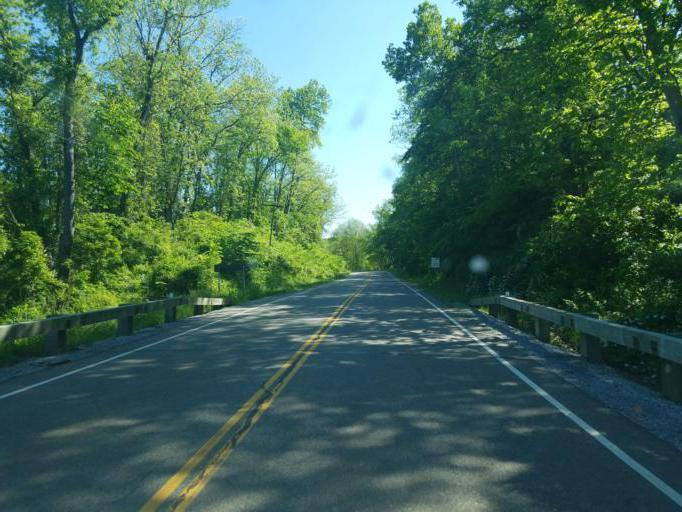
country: US
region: Ohio
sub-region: Summit County
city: Peninsula
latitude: 41.2184
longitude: -81.5519
